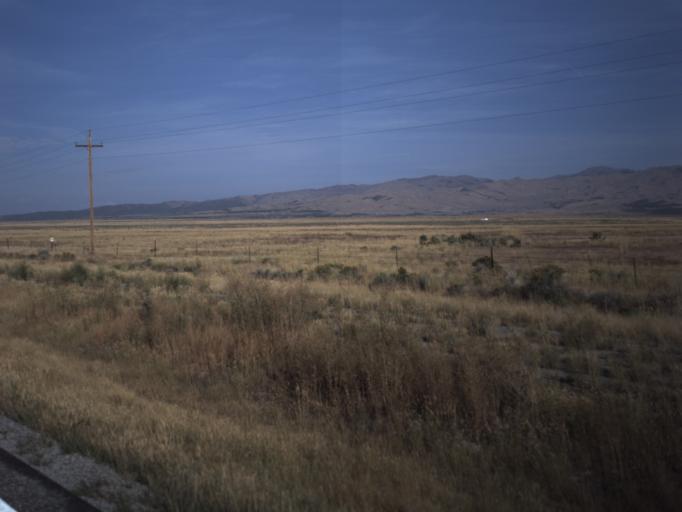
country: US
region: Idaho
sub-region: Oneida County
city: Malad City
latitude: 41.9661
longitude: -112.9631
